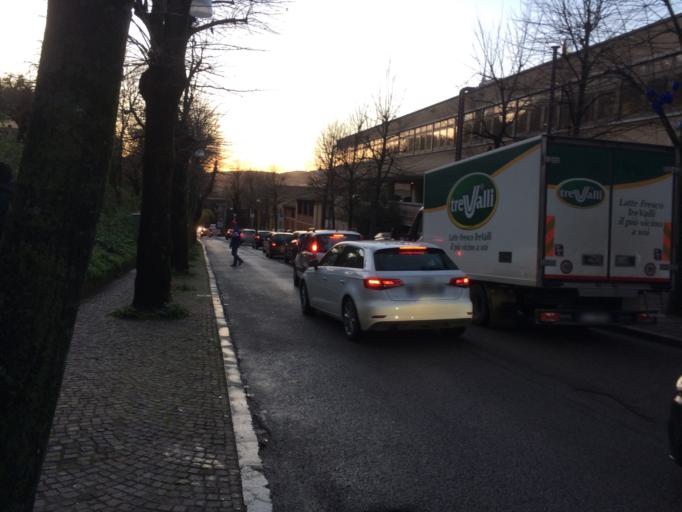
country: IT
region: Umbria
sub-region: Provincia di Perugia
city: Perugia
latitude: 43.1151
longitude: 12.3853
